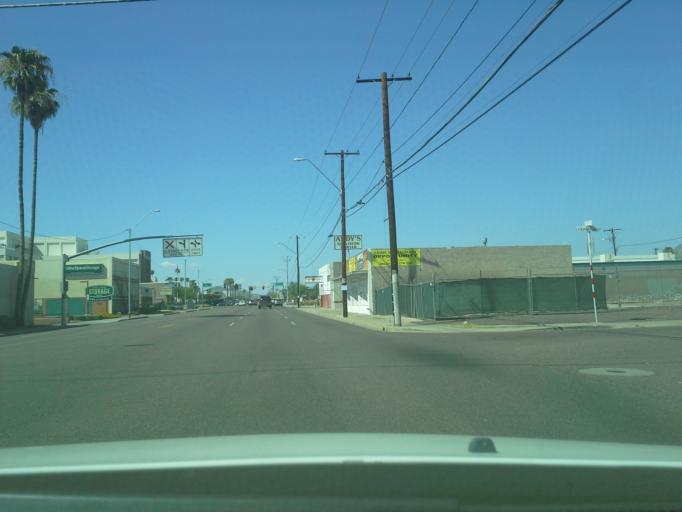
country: US
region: Arizona
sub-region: Maricopa County
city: Phoenix
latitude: 33.4927
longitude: -112.0650
